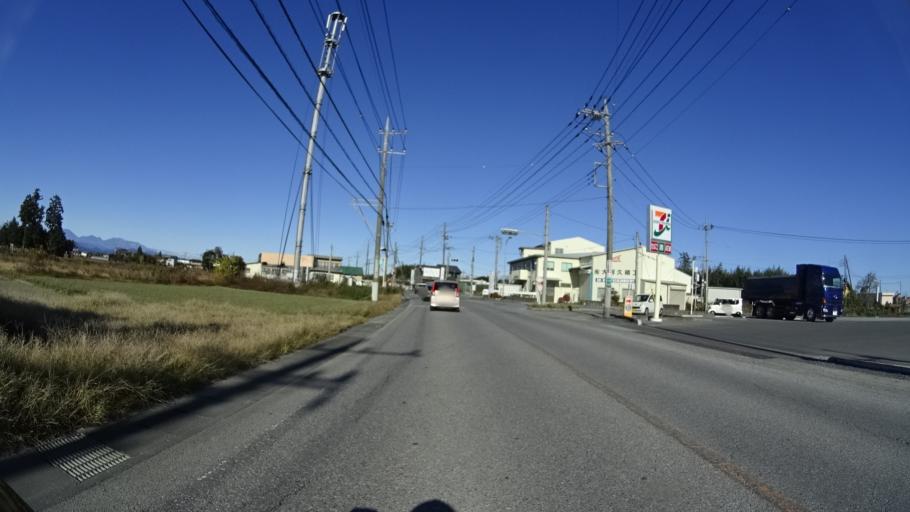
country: JP
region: Tochigi
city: Mibu
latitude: 36.4477
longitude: 139.7562
